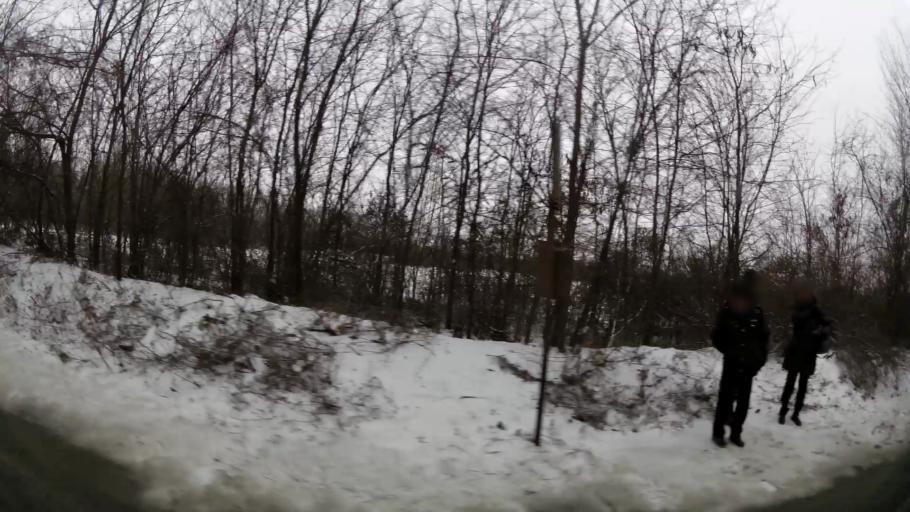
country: RO
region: Dambovita
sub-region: Comuna Ulmi
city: Ulmi
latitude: 44.8974
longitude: 25.5065
